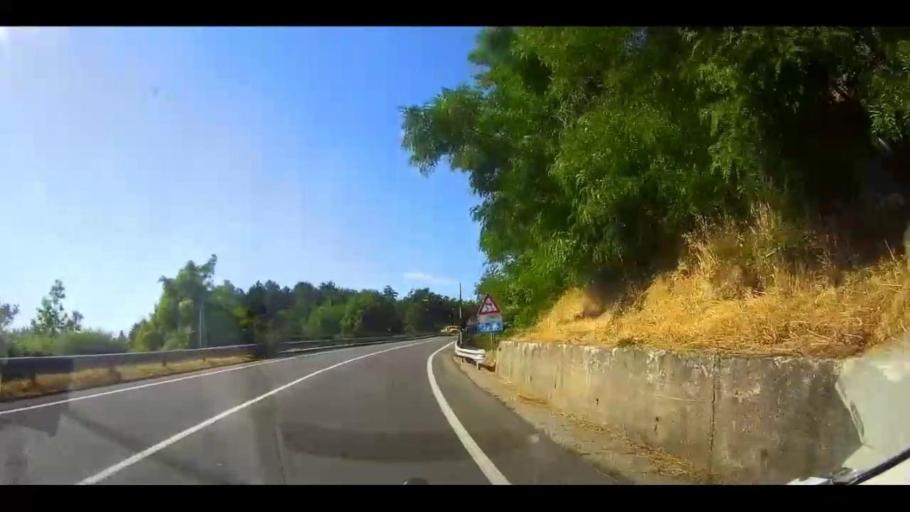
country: IT
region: Calabria
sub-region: Provincia di Cosenza
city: Celico
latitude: 39.3297
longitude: 16.3616
